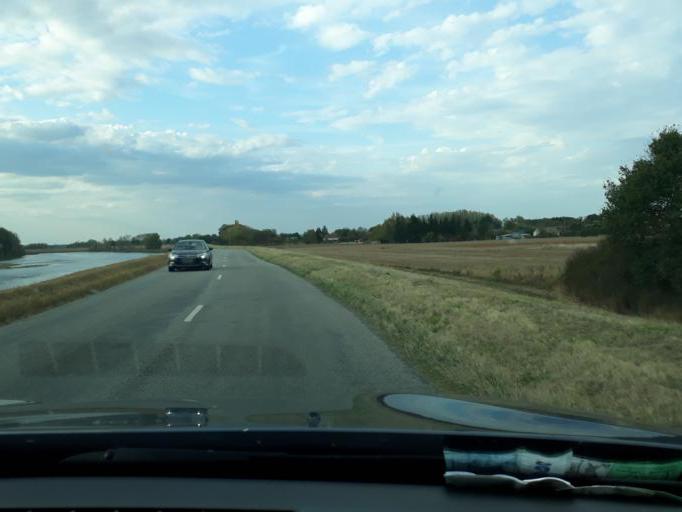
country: FR
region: Centre
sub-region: Departement du Loiret
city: Saint-Benoit-sur-Loire
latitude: 47.8236
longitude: 2.2970
